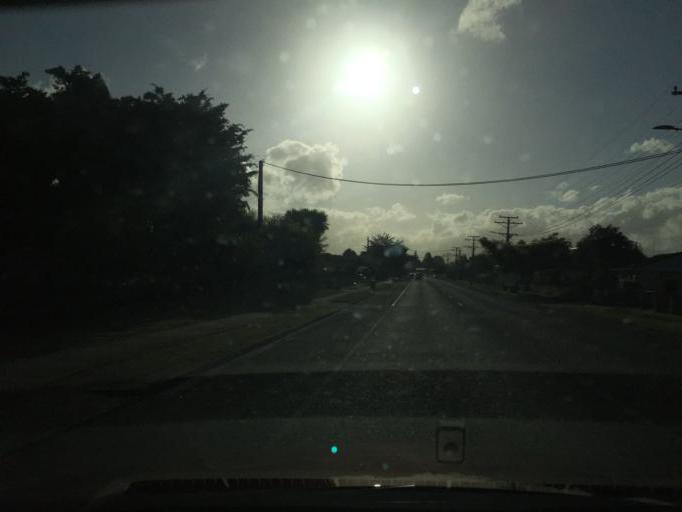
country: NZ
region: Waikato
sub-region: Waipa District
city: Cambridge
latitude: -38.0071
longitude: 175.3361
